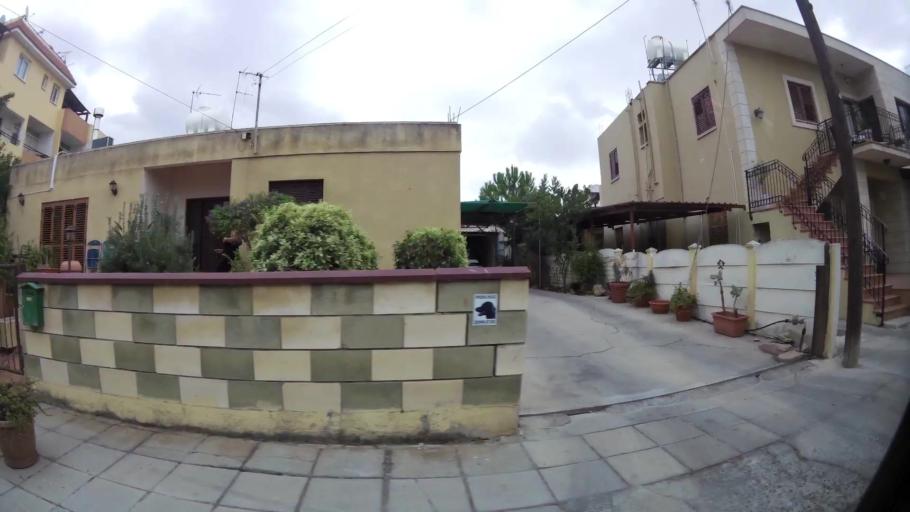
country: CY
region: Lefkosia
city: Geri
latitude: 35.1071
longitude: 33.3796
